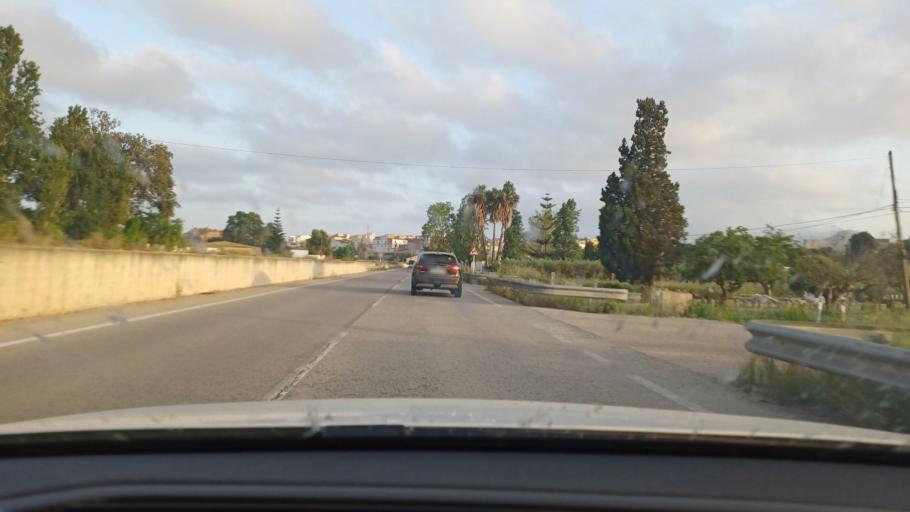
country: ES
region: Catalonia
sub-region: Provincia de Tarragona
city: Amposta
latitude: 40.7201
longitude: 0.5744
